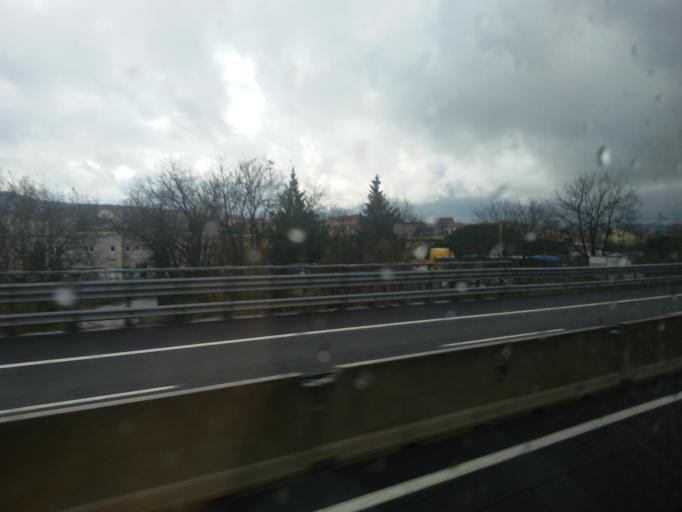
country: IT
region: Tuscany
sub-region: Province of Arezzo
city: Ponticino
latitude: 43.4820
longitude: 11.7249
